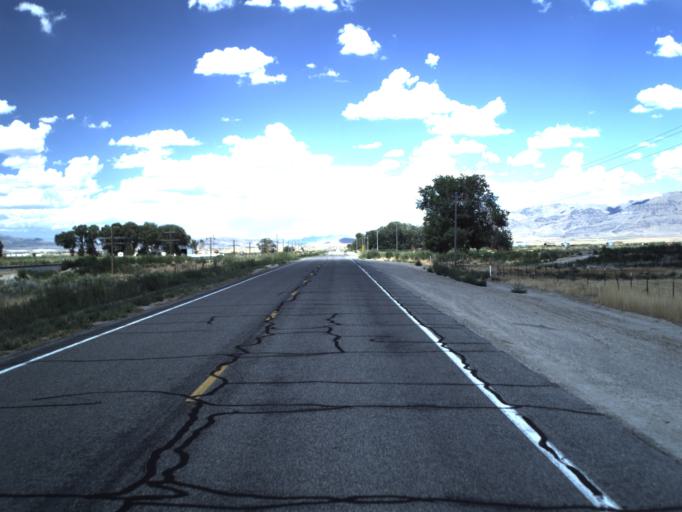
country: US
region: Utah
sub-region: Millard County
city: Delta
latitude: 39.5345
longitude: -112.3670
